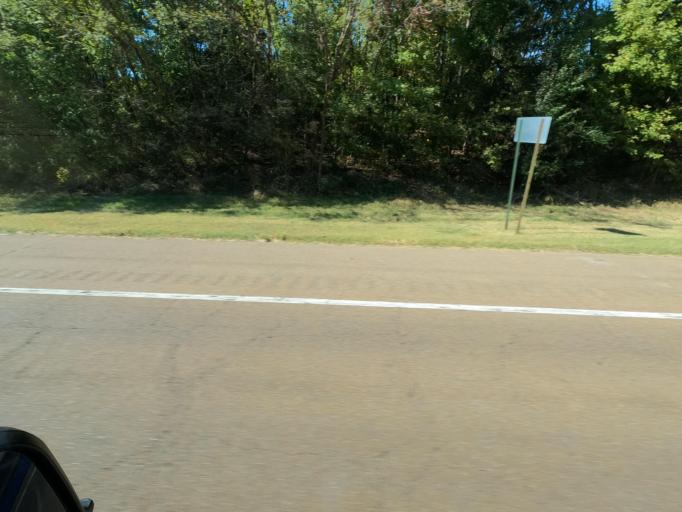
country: US
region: Tennessee
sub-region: Obion County
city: Union City
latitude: 36.4517
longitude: -89.0018
